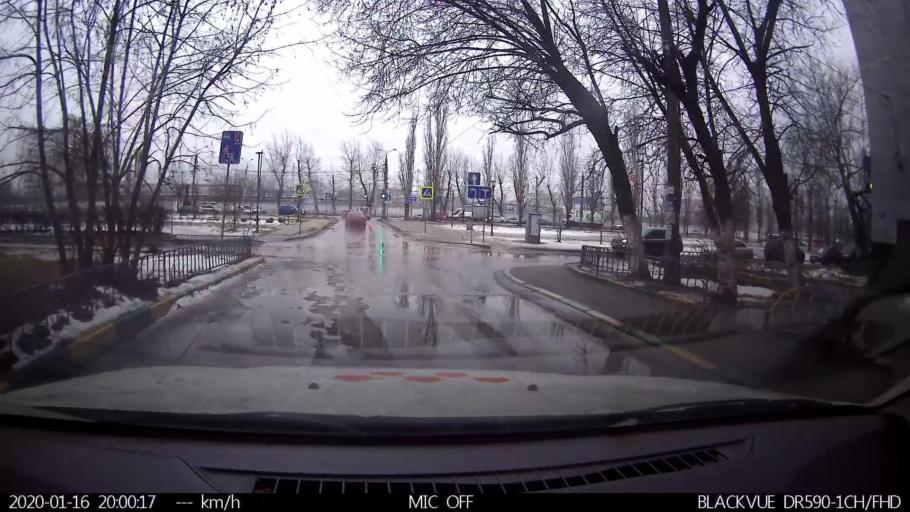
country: RU
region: Nizjnij Novgorod
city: Nizhniy Novgorod
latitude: 56.3202
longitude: 43.9372
